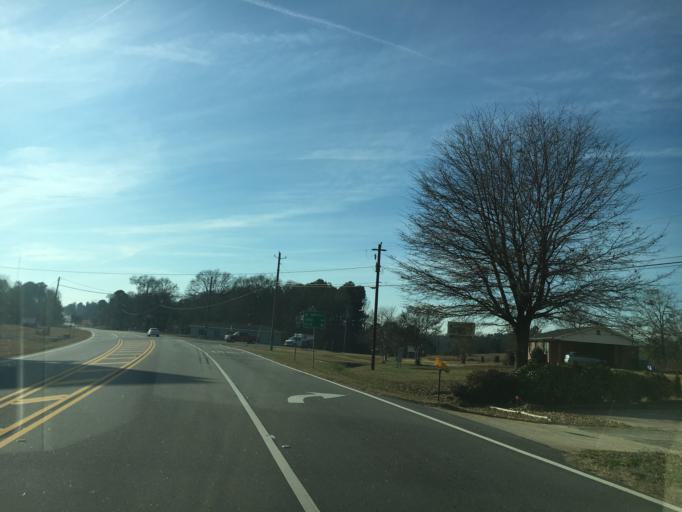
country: US
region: Georgia
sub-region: Hart County
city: Hartwell
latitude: 34.3615
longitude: -82.9671
